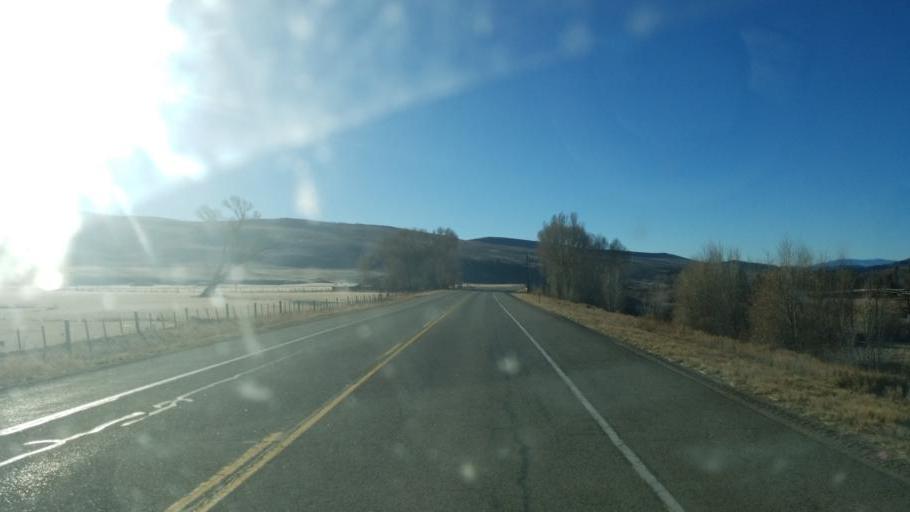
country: US
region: Colorado
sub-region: Gunnison County
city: Crested Butte
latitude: 38.7341
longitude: -106.8532
